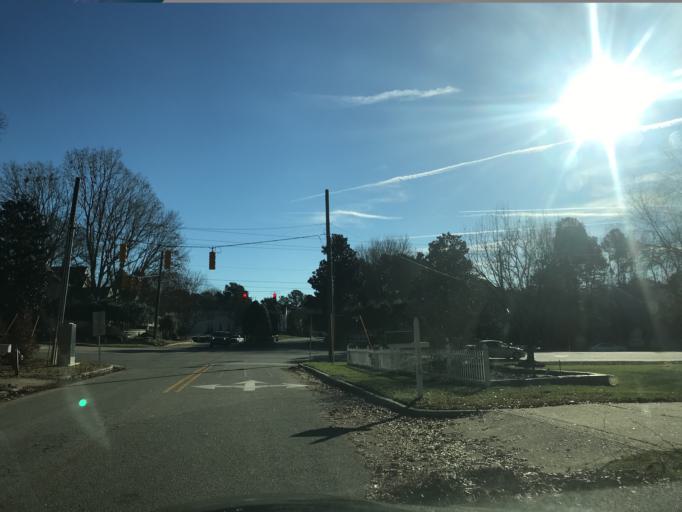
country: US
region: North Carolina
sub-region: Wake County
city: Wake Forest
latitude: 35.8958
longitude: -78.6001
